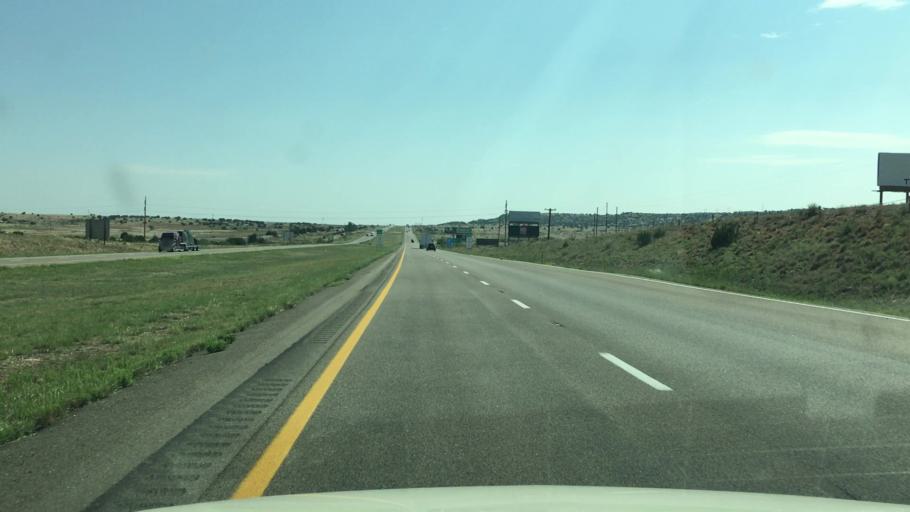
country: US
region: New Mexico
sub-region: Guadalupe County
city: Santa Rosa
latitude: 34.9503
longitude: -104.6343
